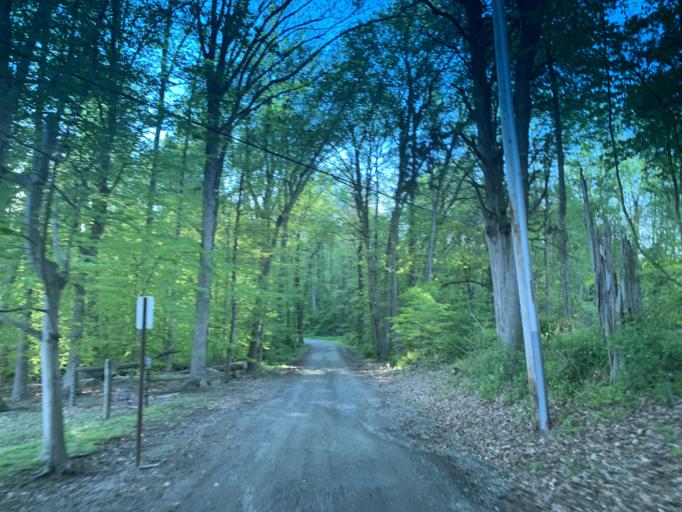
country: US
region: Maryland
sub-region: Harford County
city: Aberdeen
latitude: 39.5428
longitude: -76.1734
